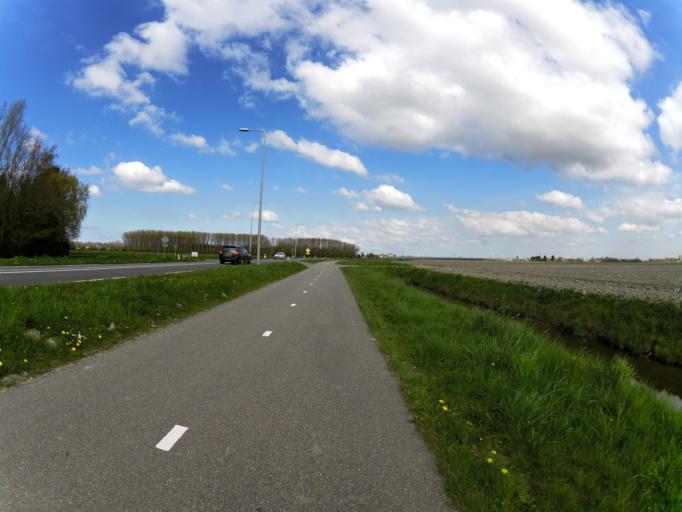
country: NL
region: South Holland
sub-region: Gemeente Hellevoetsluis
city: Nieuwenhoorn
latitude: 51.8922
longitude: 4.1037
